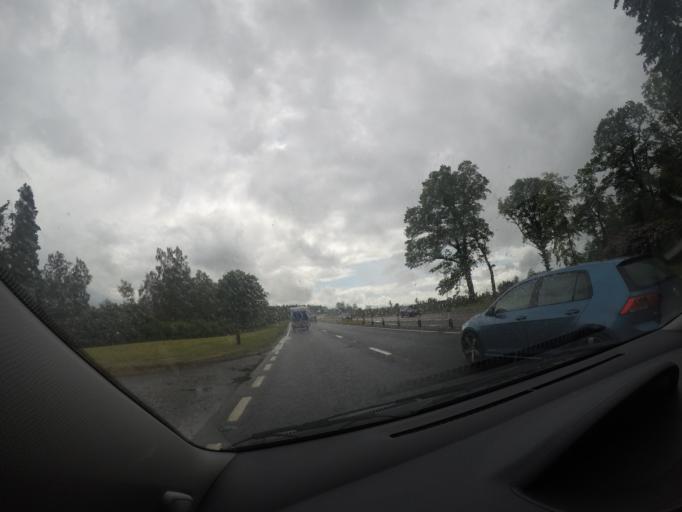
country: GB
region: Scotland
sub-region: Perth and Kinross
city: Methven
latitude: 56.3626
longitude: -3.5564
